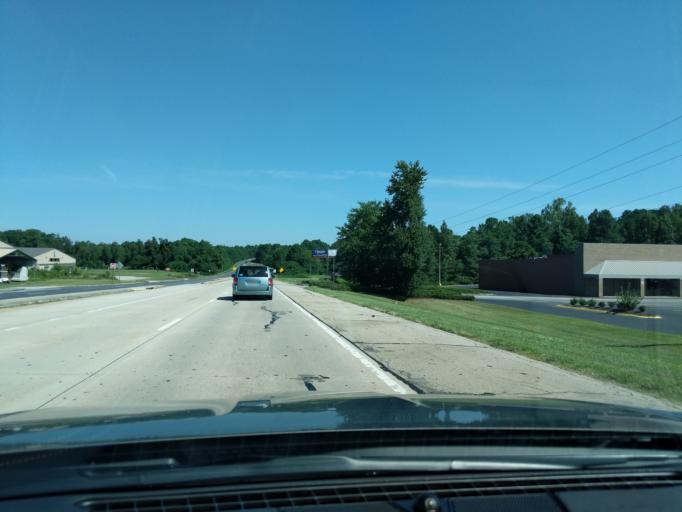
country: US
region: Georgia
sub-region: Habersham County
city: Cornelia
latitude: 34.5125
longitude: -83.5450
